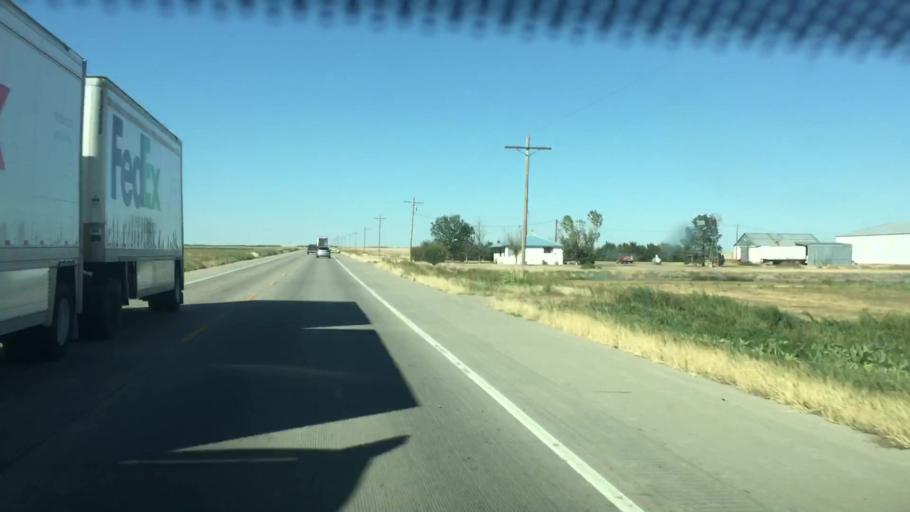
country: US
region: Colorado
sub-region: Prowers County
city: Lamar
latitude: 38.2303
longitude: -102.7240
